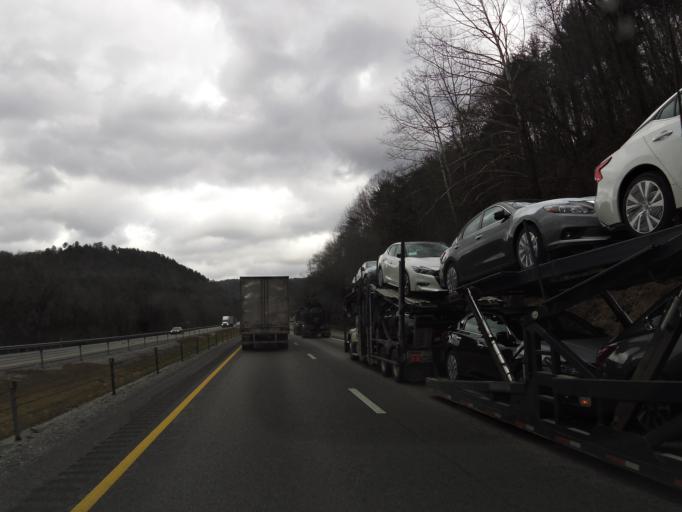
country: US
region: Georgia
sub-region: Dade County
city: Trenton
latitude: 34.9896
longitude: -85.4888
